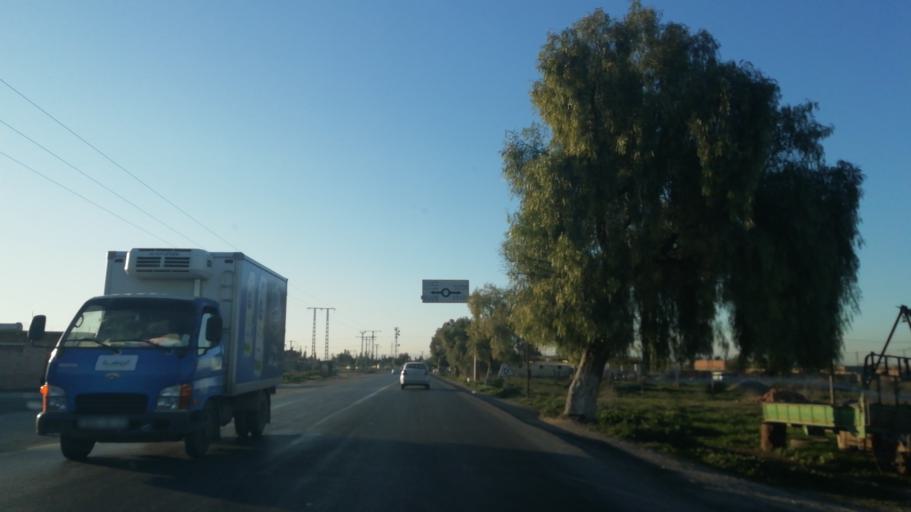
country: DZ
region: Relizane
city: Relizane
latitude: 35.7652
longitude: 0.6405
